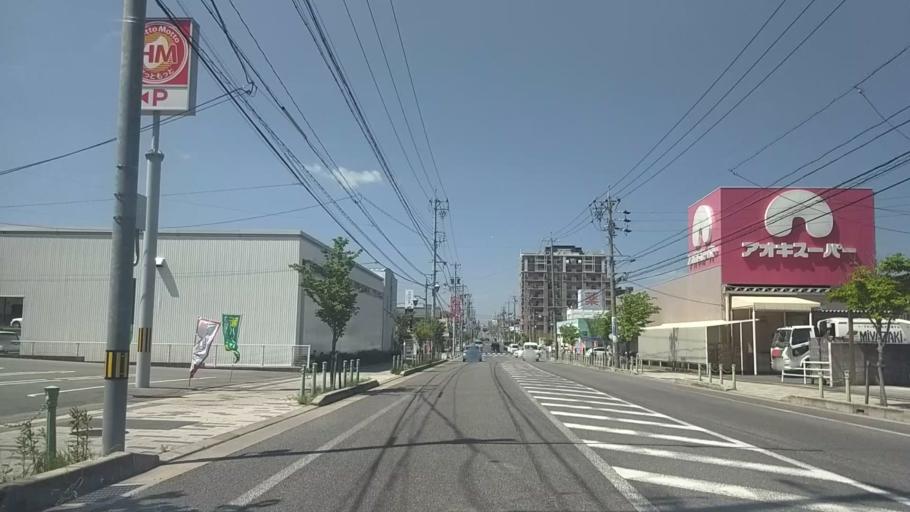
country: JP
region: Aichi
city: Okazaki
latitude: 34.9682
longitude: 137.1715
